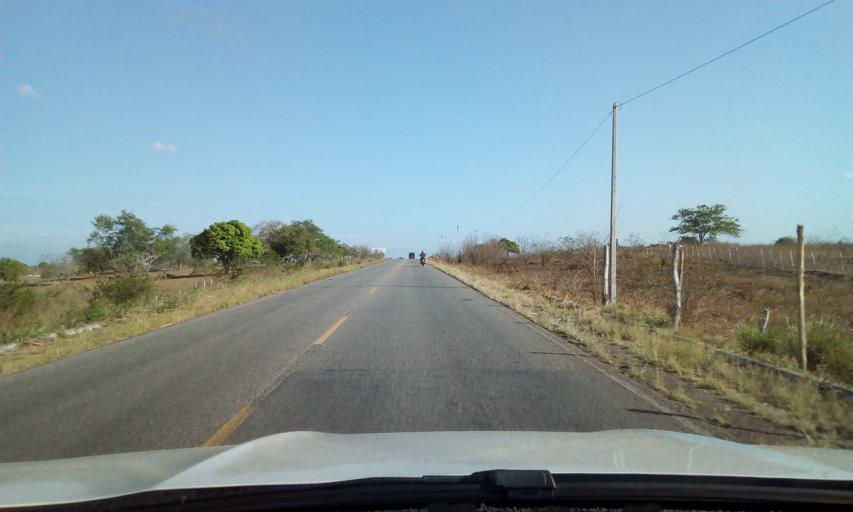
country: BR
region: Paraiba
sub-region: Guarabira
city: Guarabira
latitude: -6.9301
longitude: -35.4383
